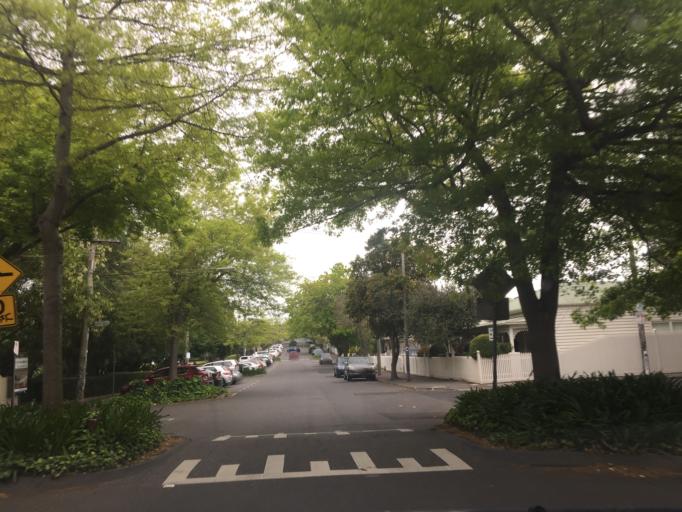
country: AU
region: Victoria
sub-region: Boroondara
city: Hawthorn East
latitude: -37.8221
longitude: 145.0425
